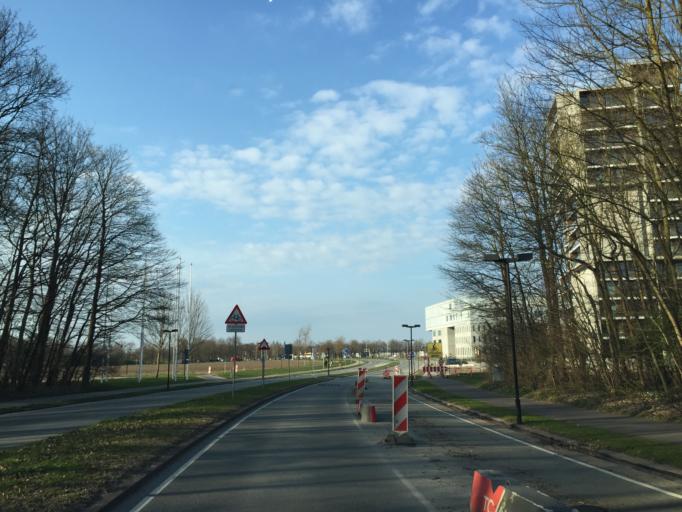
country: DK
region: South Denmark
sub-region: Odense Kommune
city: Neder Holluf
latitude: 55.3724
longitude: 10.4276
